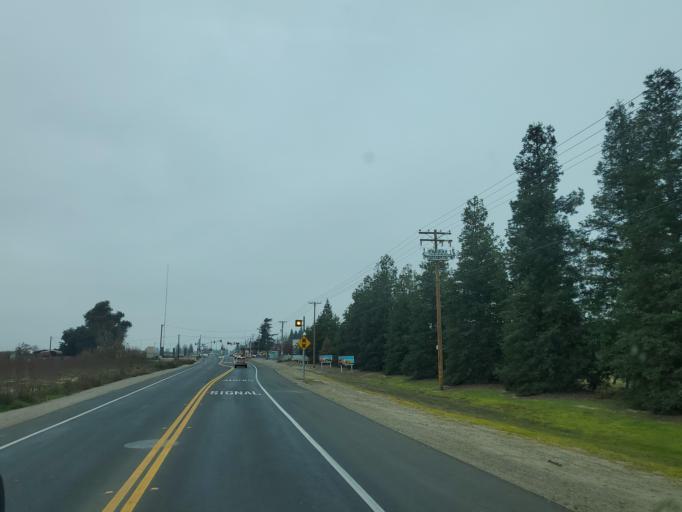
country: US
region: California
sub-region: Stanislaus County
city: Hughson
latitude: 37.5728
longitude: -120.8470
